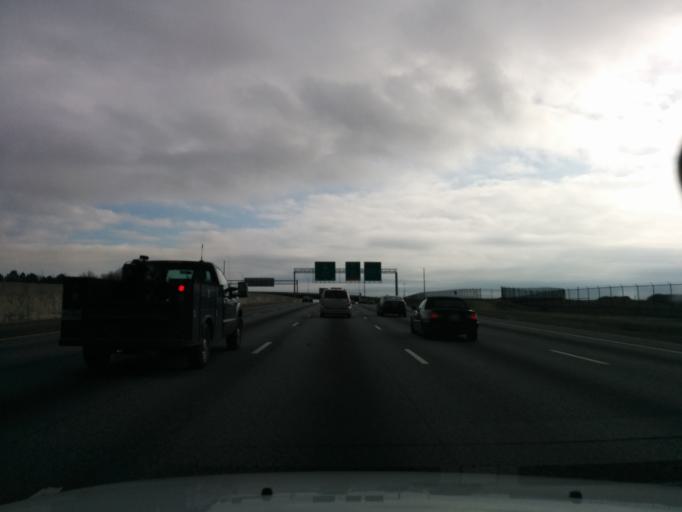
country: US
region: Georgia
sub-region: Fulton County
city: College Park
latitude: 33.6229
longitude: -84.4255
